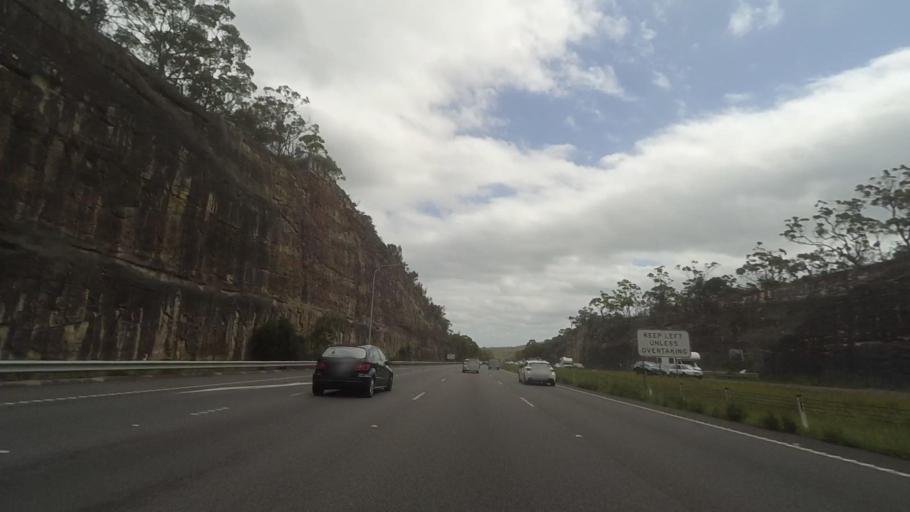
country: AU
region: New South Wales
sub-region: Gosford Shire
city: Point Clare
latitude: -33.4314
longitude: 151.2237
